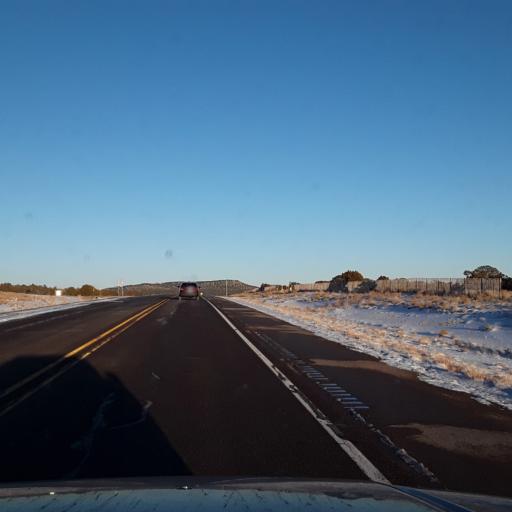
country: US
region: New Mexico
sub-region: Lincoln County
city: Carrizozo
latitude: 34.2349
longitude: -105.6165
